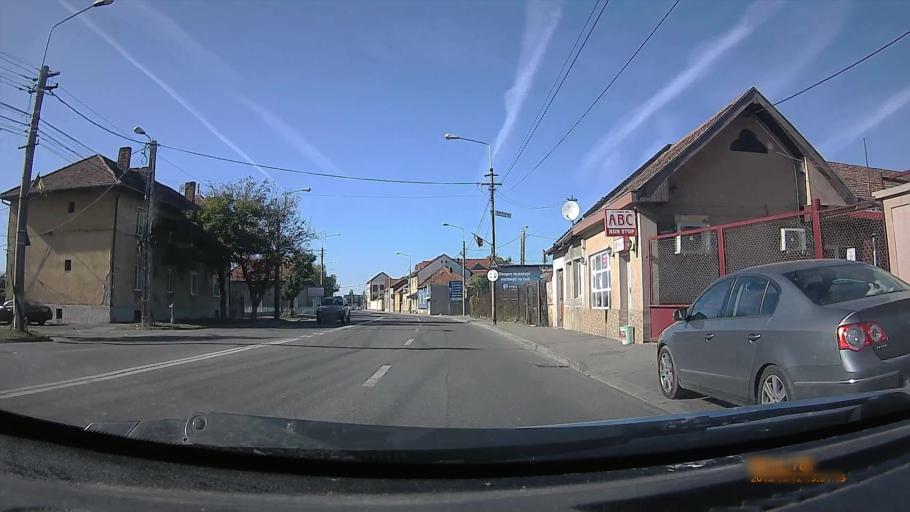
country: RO
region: Bihor
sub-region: Comuna Sanmartin
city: Sanmartin
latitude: 47.0444
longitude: 21.9696
